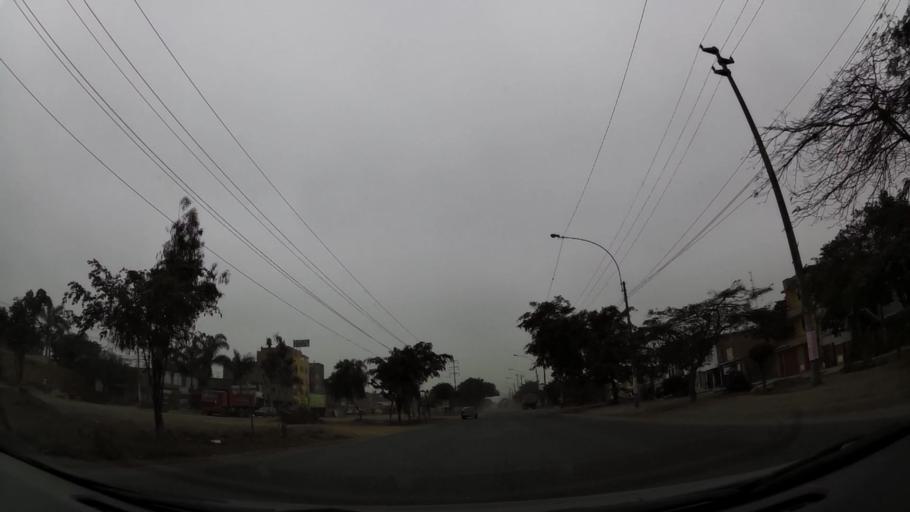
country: PE
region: Lima
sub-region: Lima
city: Urb. Santo Domingo
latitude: -11.9169
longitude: -77.0596
